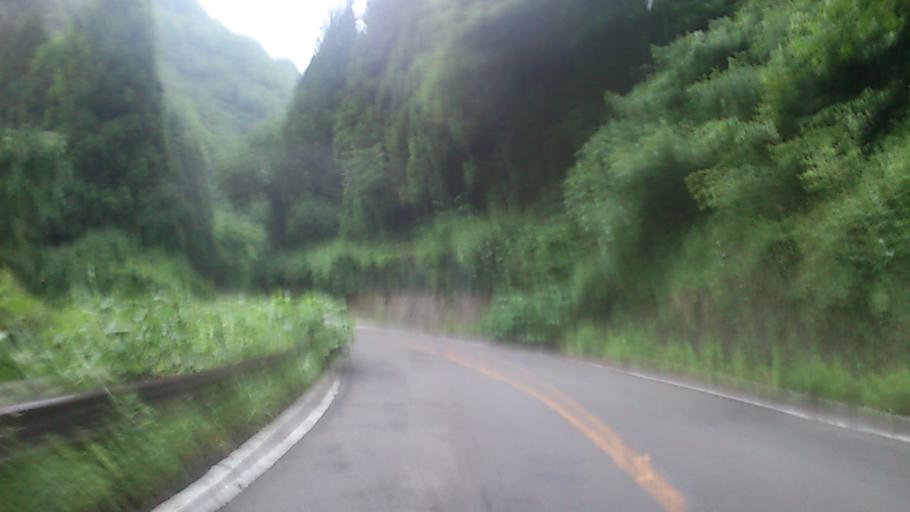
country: JP
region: Fukushima
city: Fukushima-shi
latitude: 37.7499
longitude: 140.3339
